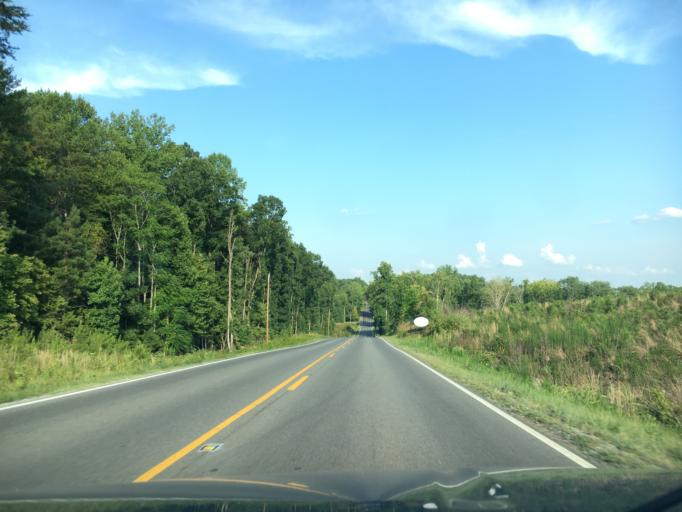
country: US
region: Virginia
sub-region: Franklin County
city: Union Hall
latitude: 36.9742
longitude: -79.6101
